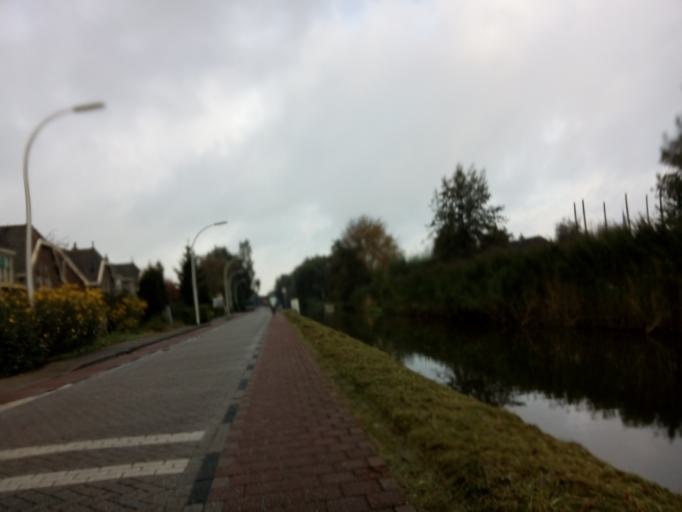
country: NL
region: South Holland
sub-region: Gemeente Maassluis
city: Maassluis
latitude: 51.9290
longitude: 4.2705
